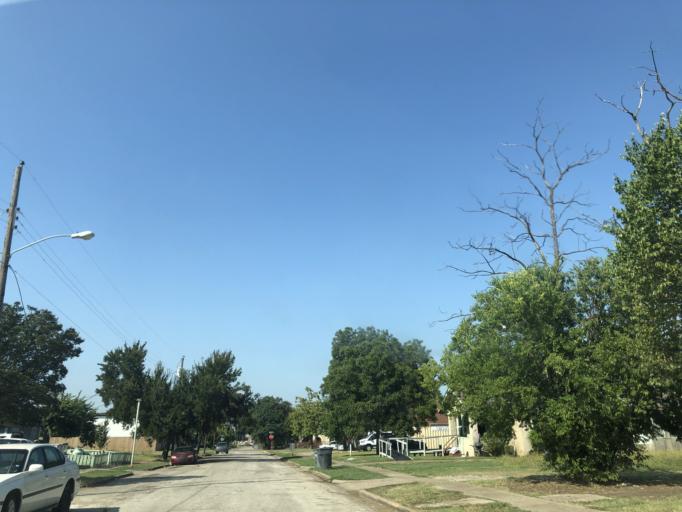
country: US
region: Texas
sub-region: Dallas County
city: Dallas
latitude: 32.7662
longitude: -96.7700
